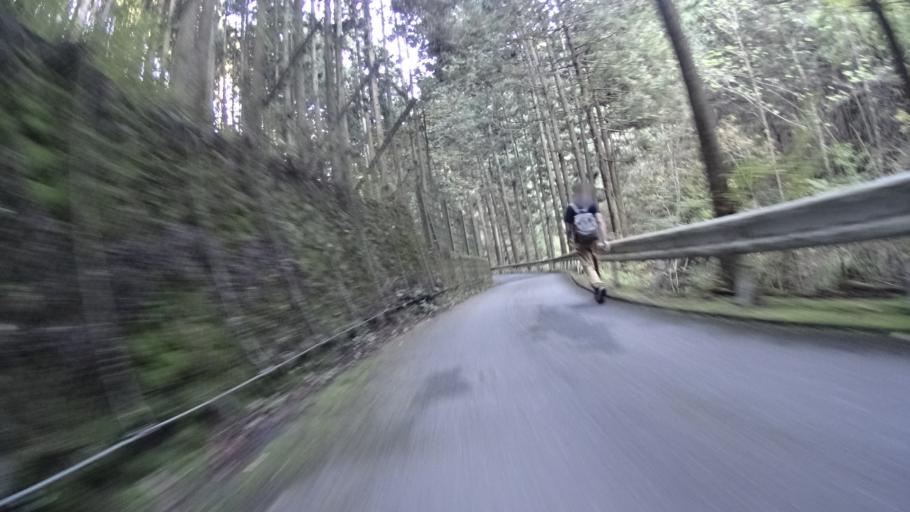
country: JP
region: Tokyo
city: Itsukaichi
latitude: 35.6613
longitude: 139.1805
